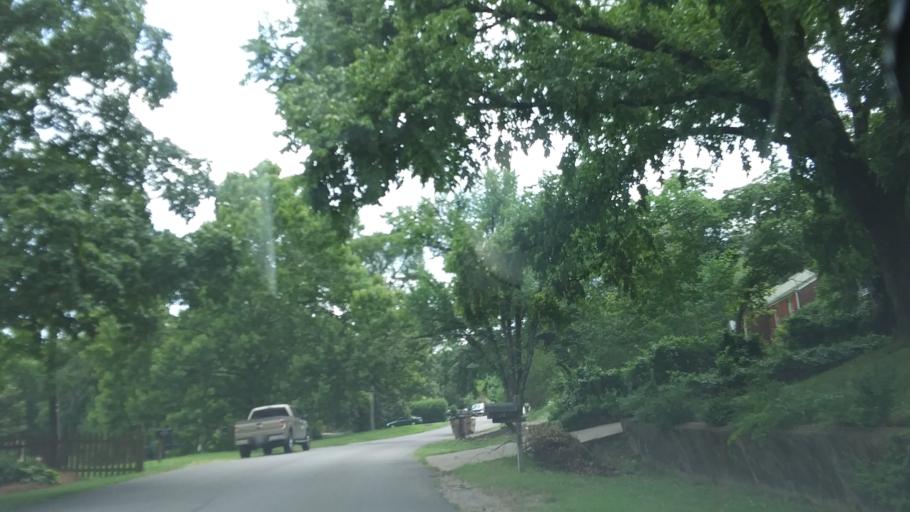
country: US
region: Tennessee
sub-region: Davidson County
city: Belle Meade
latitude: 36.1355
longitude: -86.8625
